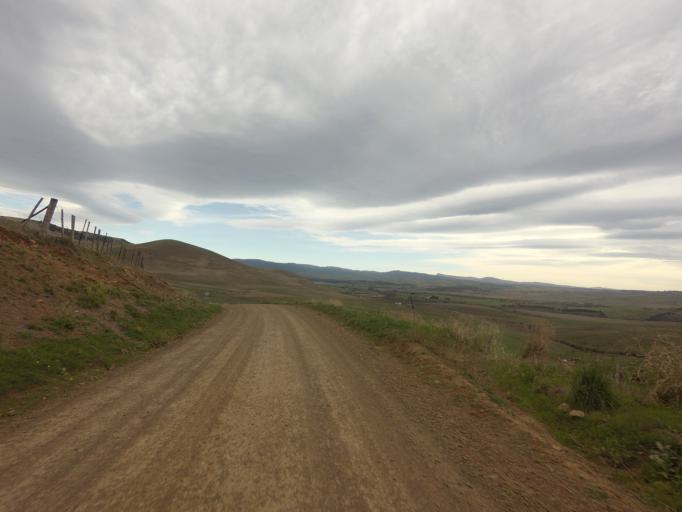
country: AU
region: Tasmania
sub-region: Derwent Valley
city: New Norfolk
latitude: -42.4550
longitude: 146.7642
